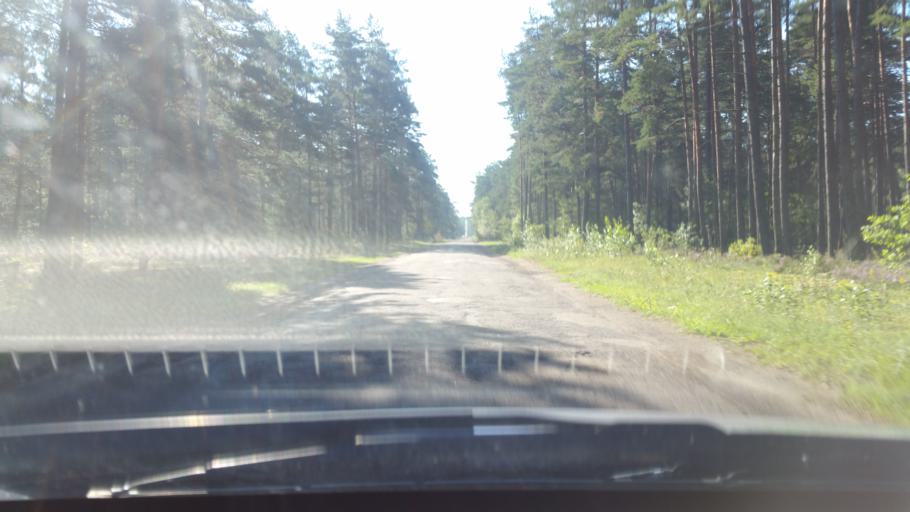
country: LV
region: Adazi
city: Adazi
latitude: 57.0975
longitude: 24.3534
